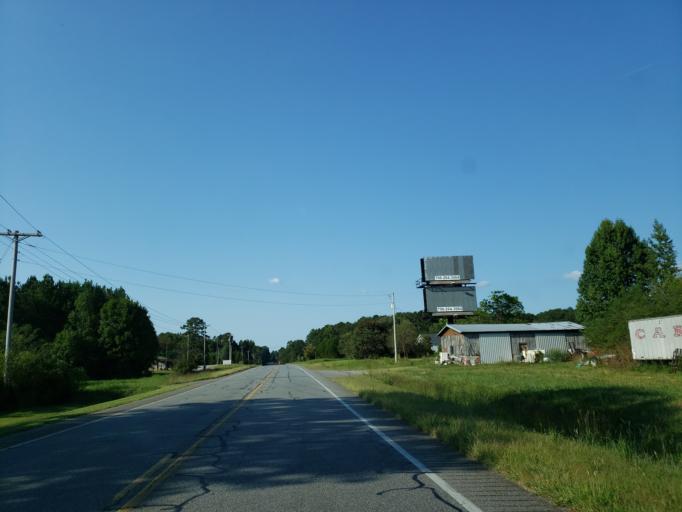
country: US
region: Tennessee
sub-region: Bradley County
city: Wildwood Lake
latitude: 34.9669
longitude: -84.7330
